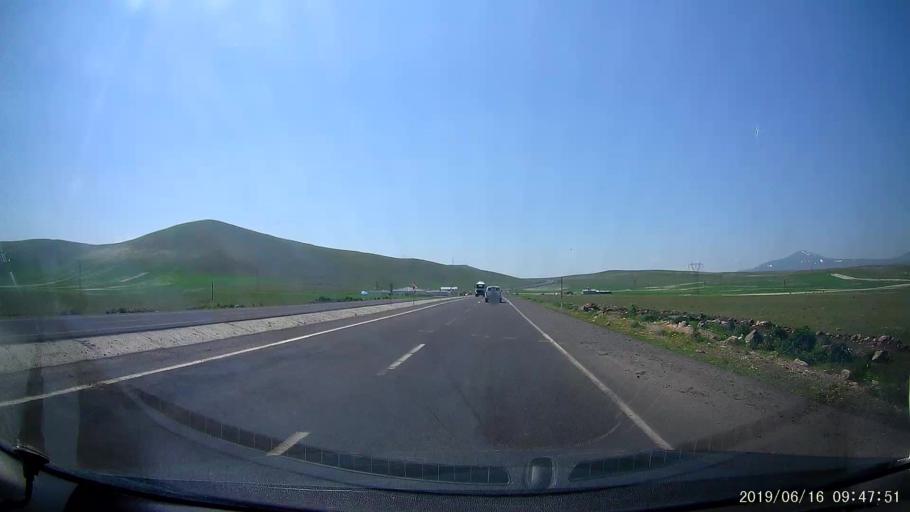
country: TR
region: Kars
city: Digor
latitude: 40.4404
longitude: 43.3485
